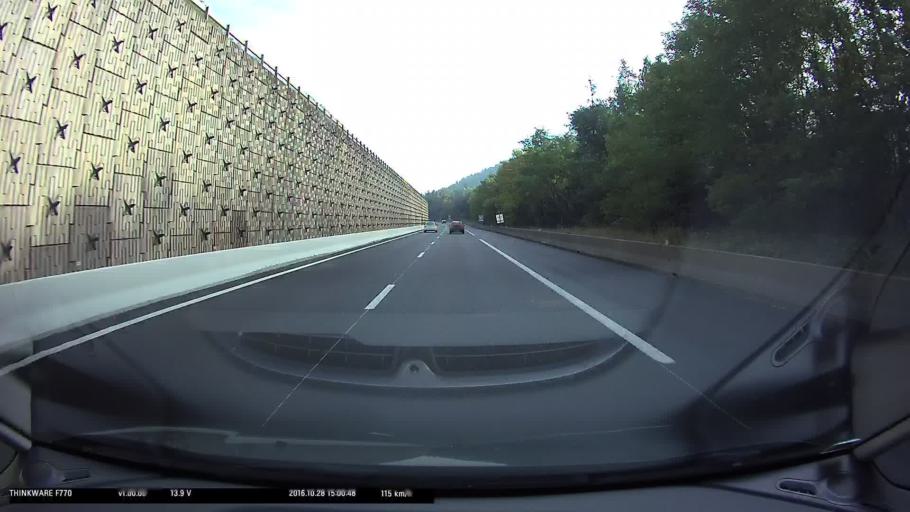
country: FR
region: Alsace
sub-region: Departement du Bas-Rhin
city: Saverne
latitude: 48.7671
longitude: 7.3395
